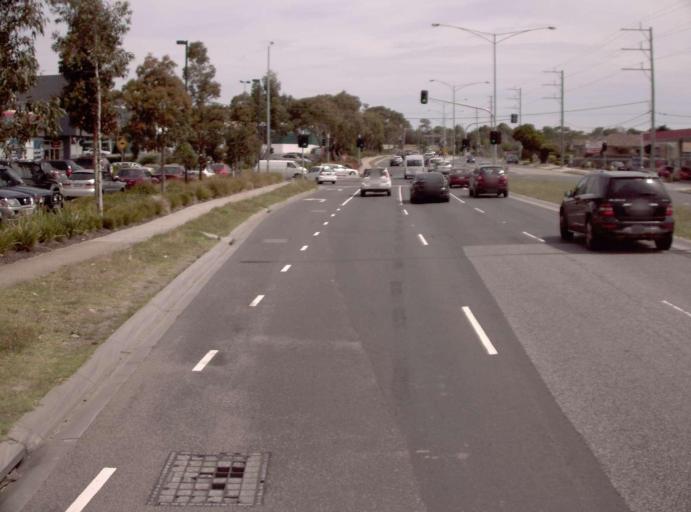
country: AU
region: Victoria
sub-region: Frankston
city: Frankston
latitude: -38.1483
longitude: 145.1352
